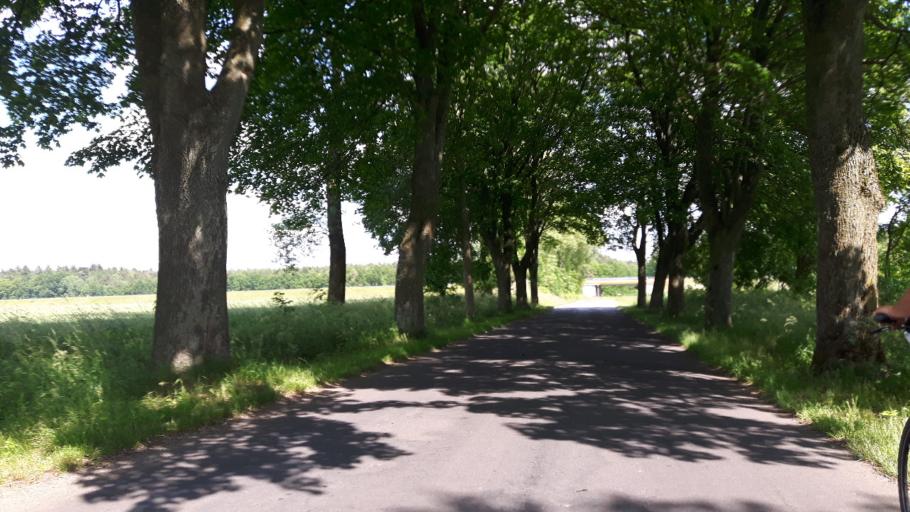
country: PL
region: West Pomeranian Voivodeship
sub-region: Powiat goleniowski
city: Nowogard
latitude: 53.6724
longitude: 15.0754
